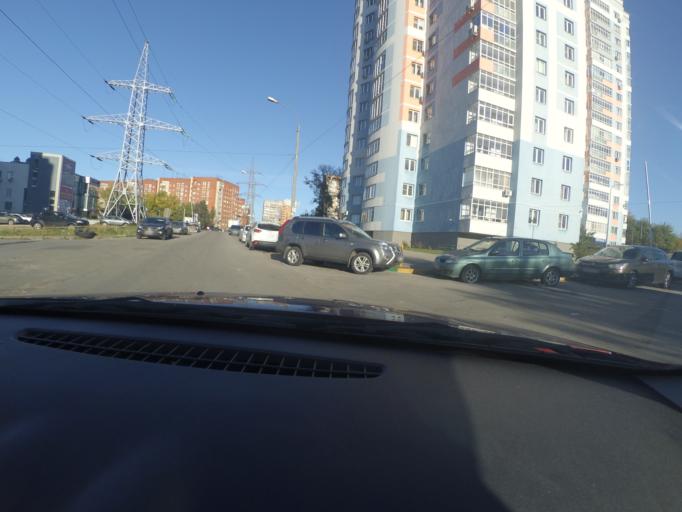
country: RU
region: Nizjnij Novgorod
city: Bor
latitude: 56.3130
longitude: 44.0699
